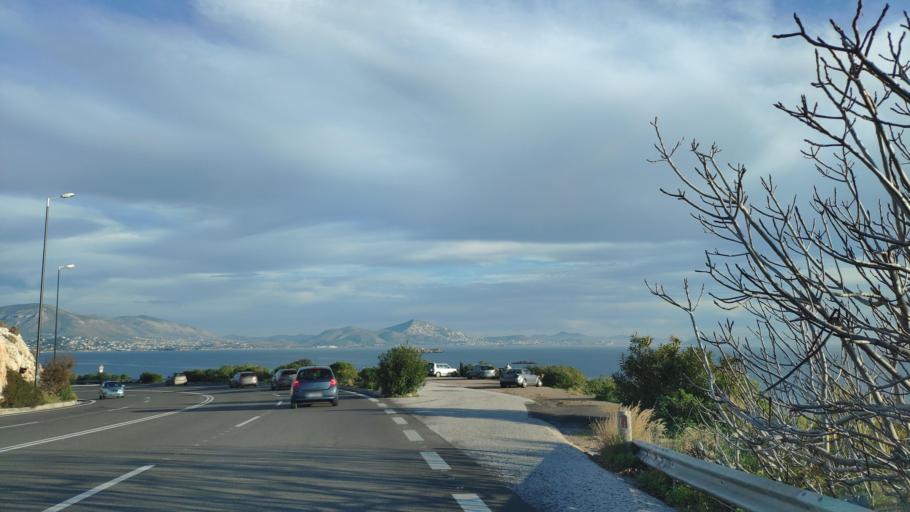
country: GR
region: Attica
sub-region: Nomarchia Anatolikis Attikis
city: Vouliagmeni
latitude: 37.7969
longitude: 23.7999
